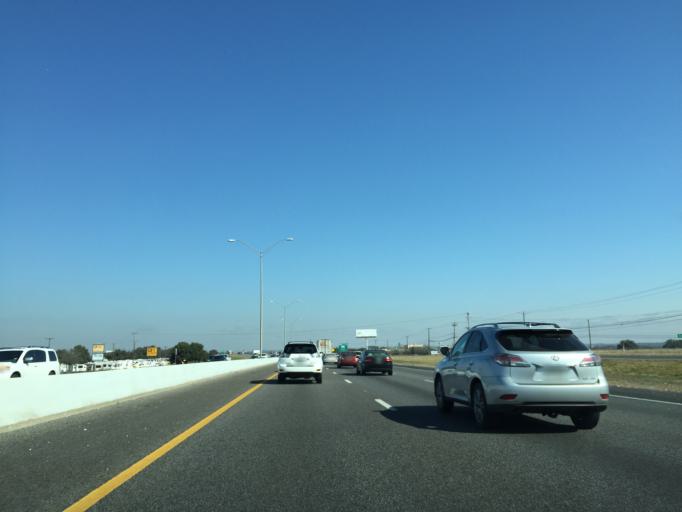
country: US
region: Texas
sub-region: Williamson County
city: Georgetown
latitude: 30.6000
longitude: -97.6882
